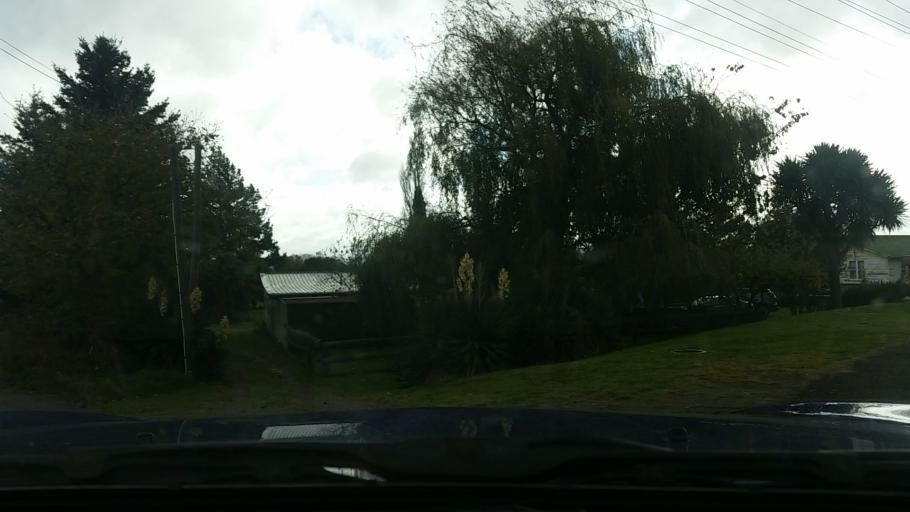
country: NZ
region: Bay of Plenty
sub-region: Rotorua District
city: Rotorua
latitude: -38.0796
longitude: 176.3244
